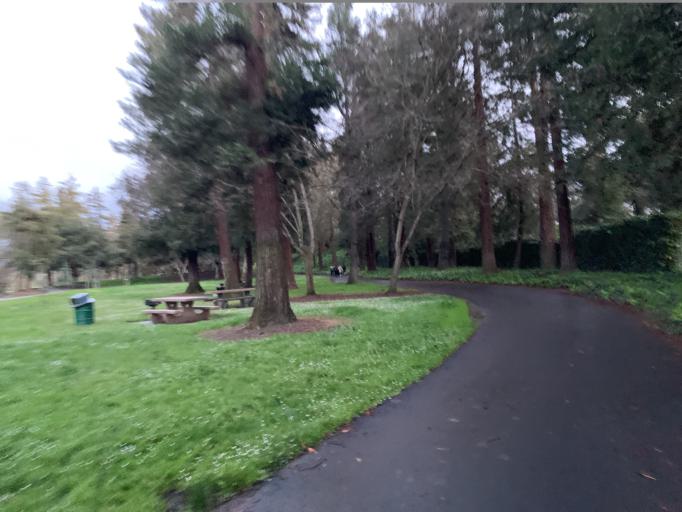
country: US
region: California
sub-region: Santa Clara County
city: San Jose
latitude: 37.3227
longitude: -121.8609
